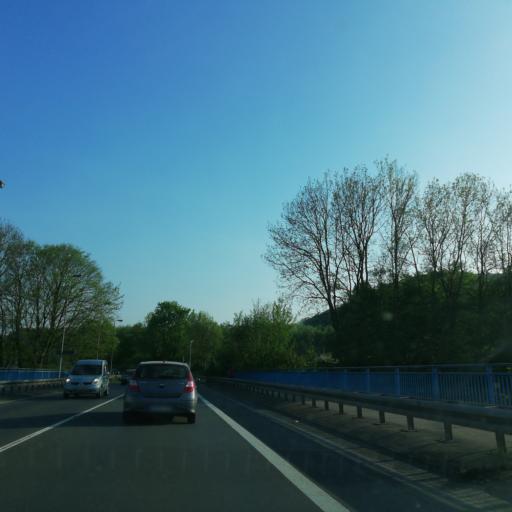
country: DE
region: North Rhine-Westphalia
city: Herdecke
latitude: 51.3948
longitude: 7.4321
